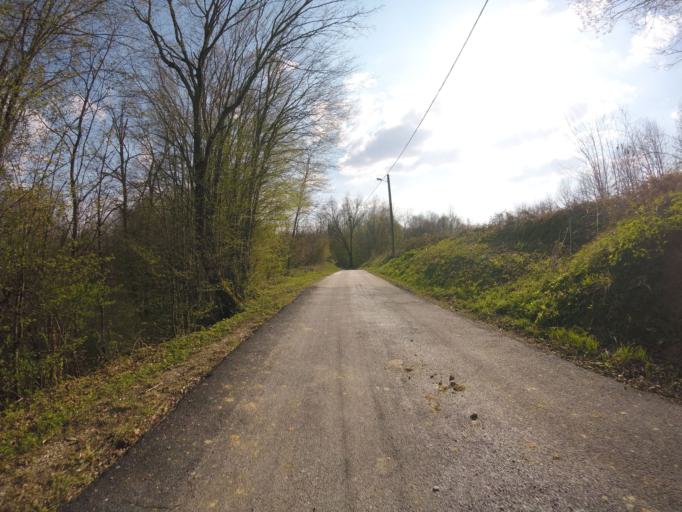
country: HR
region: Sisacko-Moslavacka
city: Glina
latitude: 45.4931
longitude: 16.0015
